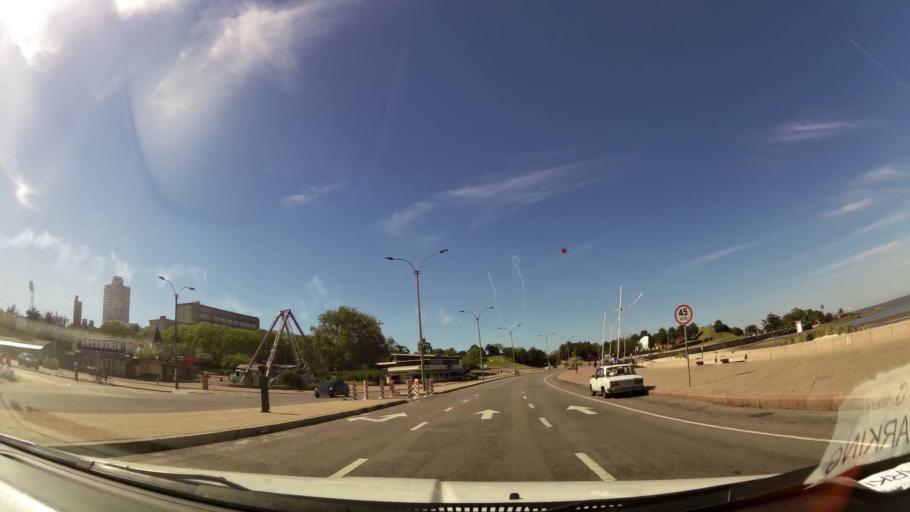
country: UY
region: Montevideo
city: Montevideo
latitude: -34.9164
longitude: -56.1693
